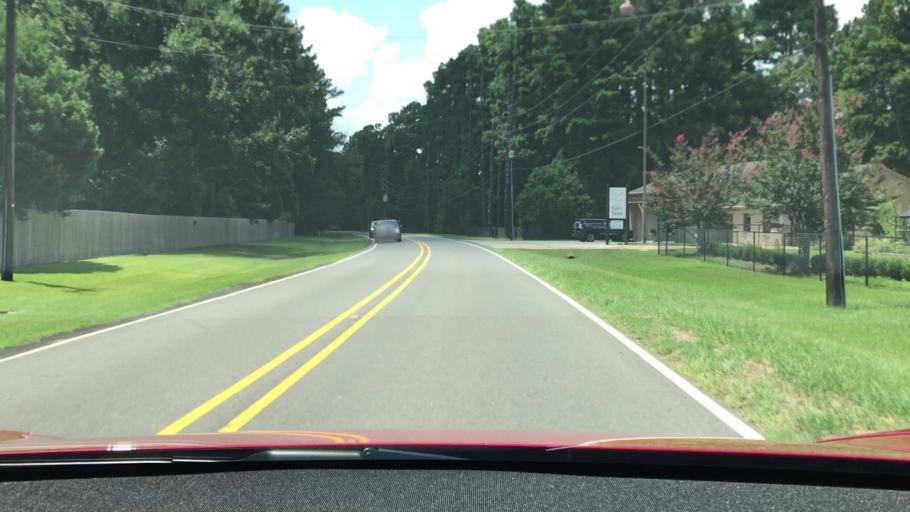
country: US
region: Louisiana
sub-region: De Soto Parish
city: Stonewall
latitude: 32.3688
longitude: -93.7032
